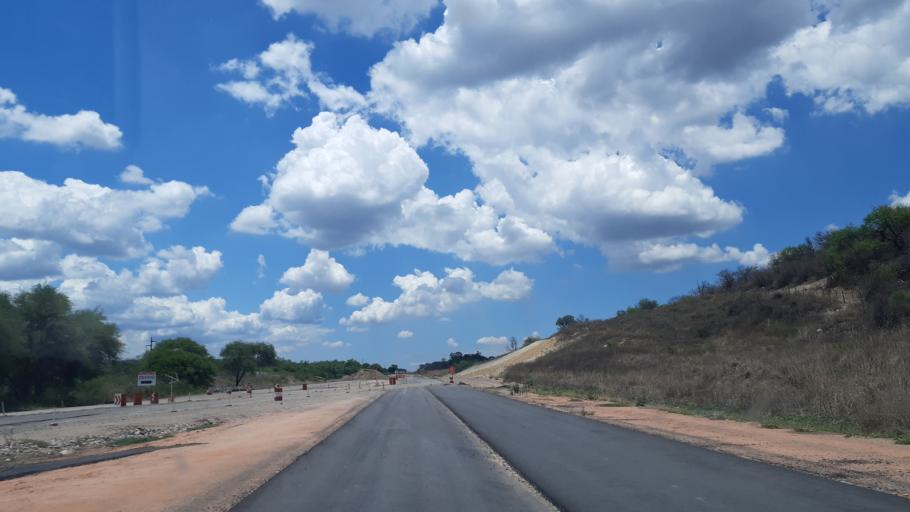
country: AR
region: Jujuy
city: La Mendieta
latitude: -24.4241
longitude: -65.0036
